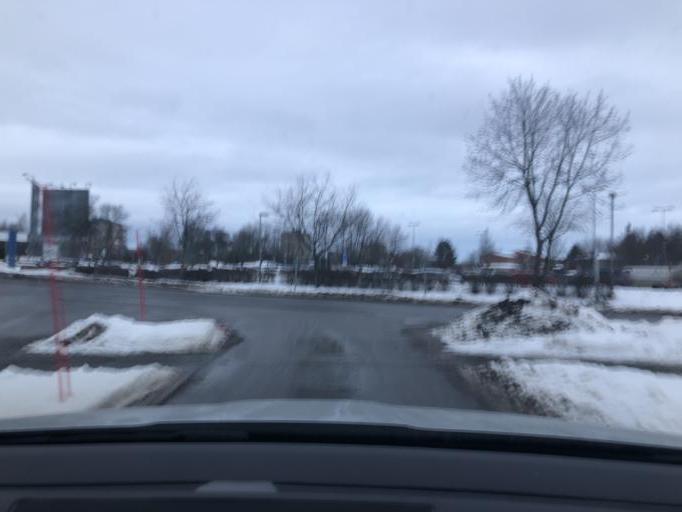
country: SE
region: OEstergoetland
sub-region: Norrkopings Kommun
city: Norrkoping
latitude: 58.5640
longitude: 16.1749
